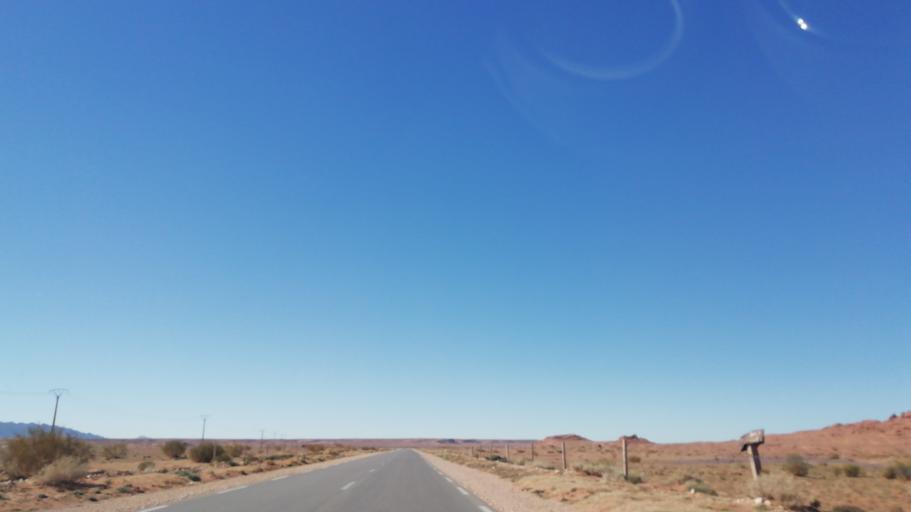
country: DZ
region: El Bayadh
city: El Abiodh Sidi Cheikh
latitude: 33.1747
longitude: 0.5256
